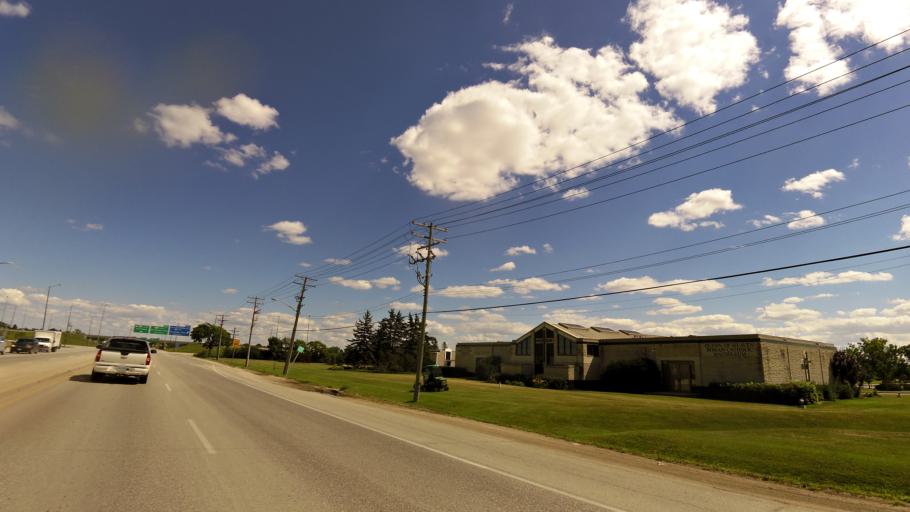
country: CA
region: Manitoba
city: Headingley
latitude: 49.8798
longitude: -97.3317
